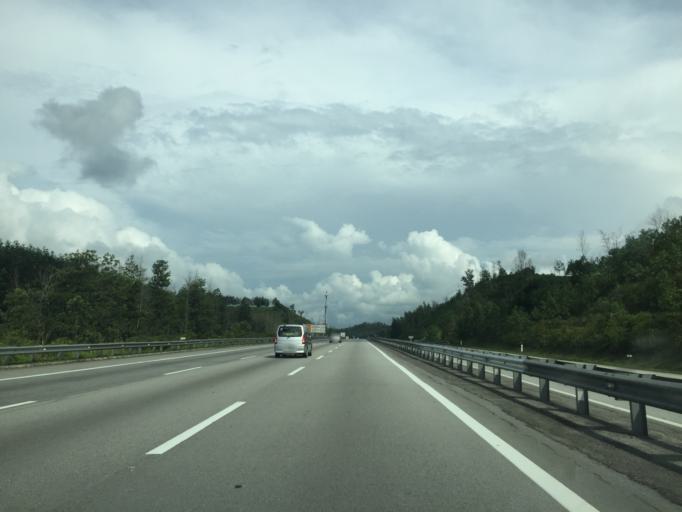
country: MY
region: Selangor
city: Batang Berjuntai
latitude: 3.5303
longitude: 101.5220
